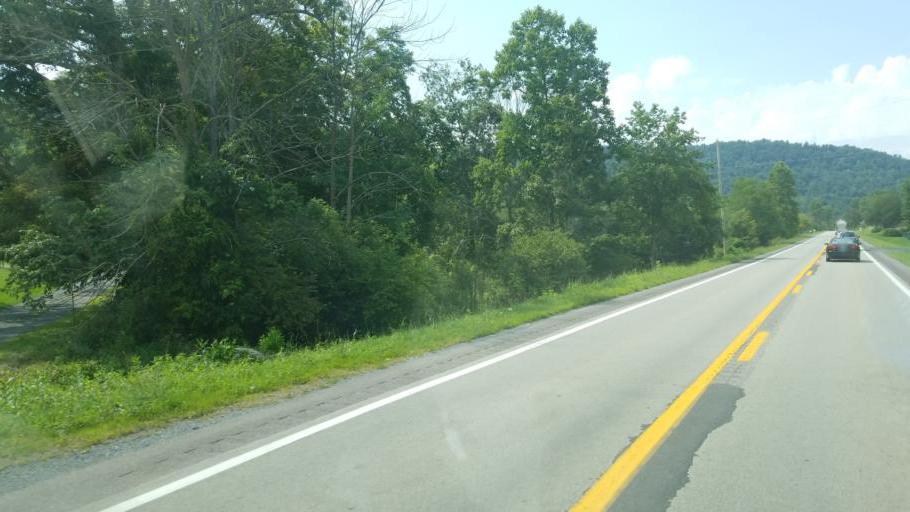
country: US
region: Virginia
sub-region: Frederick County
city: Shawnee Land
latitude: 39.3854
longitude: -78.3721
